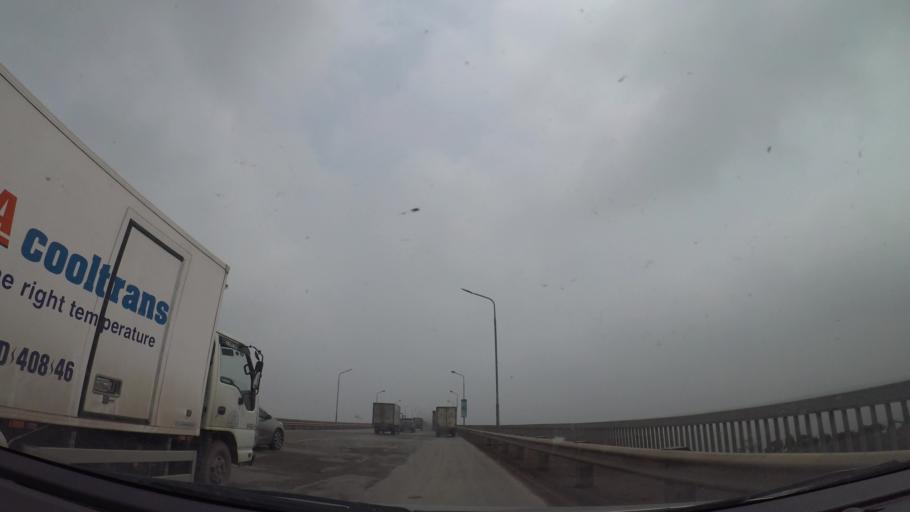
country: VN
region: Ha Noi
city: Tay Ho
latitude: 21.0925
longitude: 105.7862
